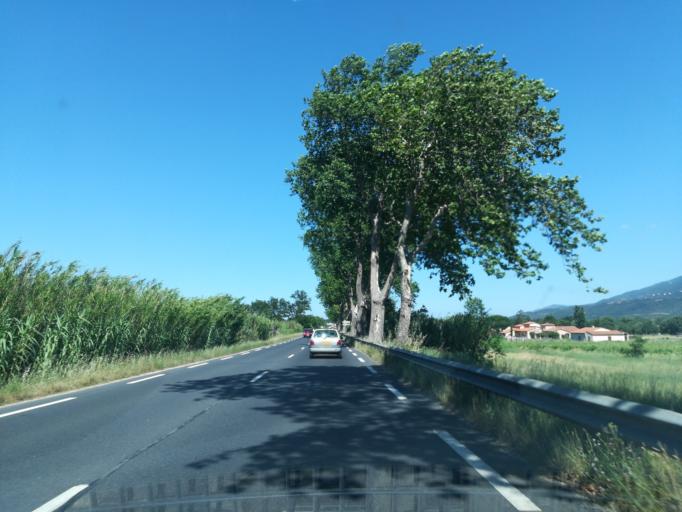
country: FR
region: Languedoc-Roussillon
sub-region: Departement des Pyrenees-Orientales
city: Sant Joan de Pladecorts
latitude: 42.5185
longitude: 2.7967
